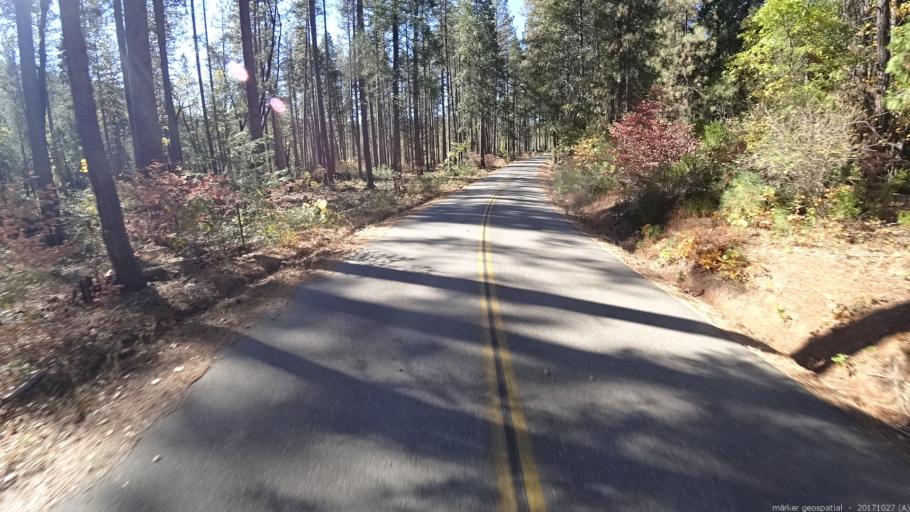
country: US
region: California
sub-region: Shasta County
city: Shingletown
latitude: 40.7367
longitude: -121.9461
